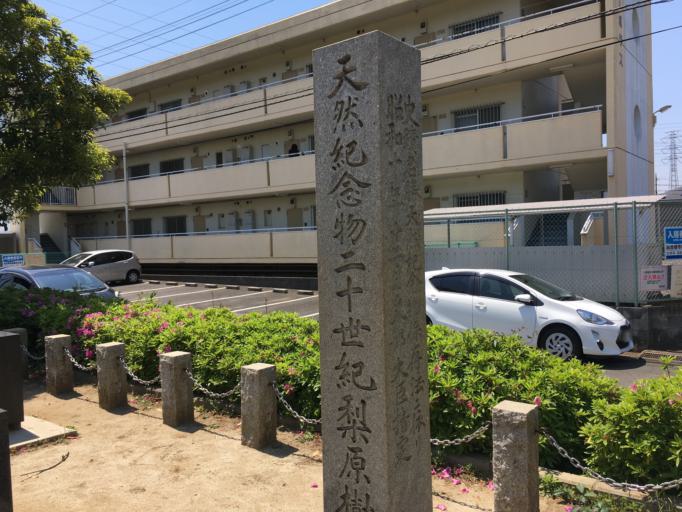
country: JP
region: Chiba
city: Matsudo
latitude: 35.7707
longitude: 139.9138
